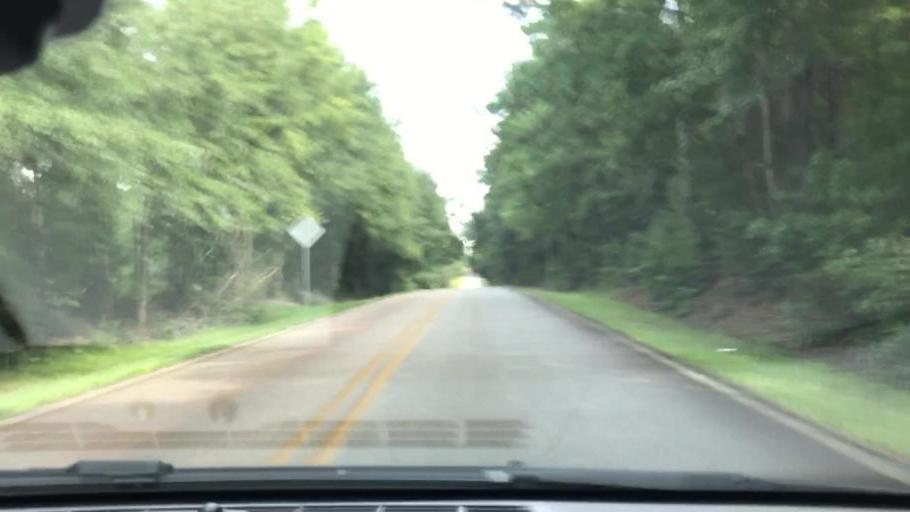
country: US
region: Georgia
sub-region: Clay County
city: Fort Gaines
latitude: 31.5707
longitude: -85.0005
